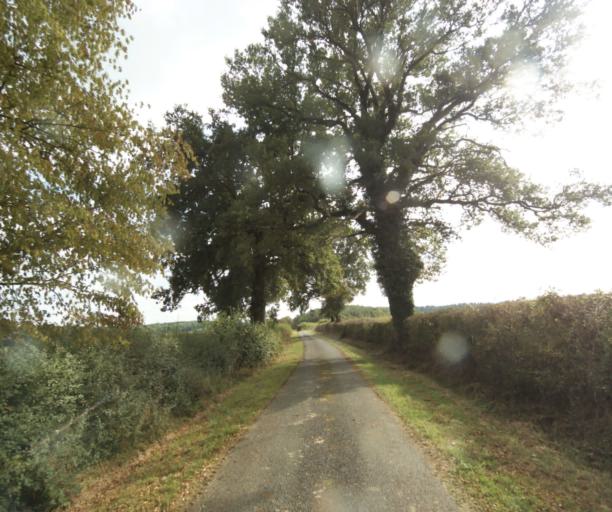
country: FR
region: Bourgogne
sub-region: Departement de Saone-et-Loire
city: Palinges
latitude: 46.5180
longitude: 4.2462
